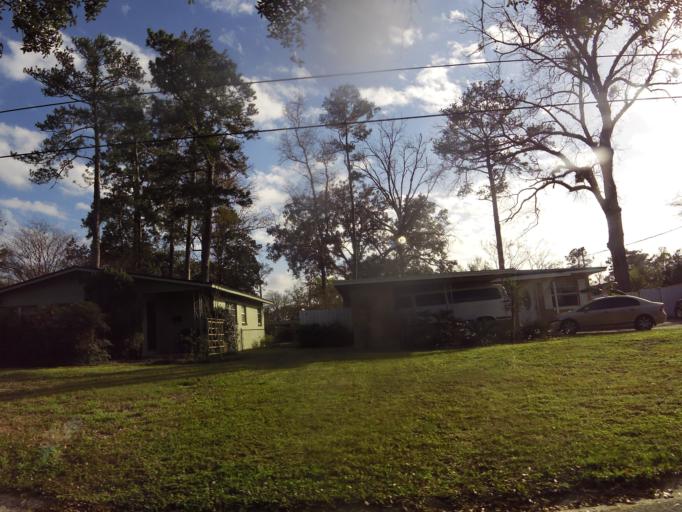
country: US
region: Florida
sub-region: Duval County
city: Jacksonville
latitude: 30.2844
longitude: -81.6143
